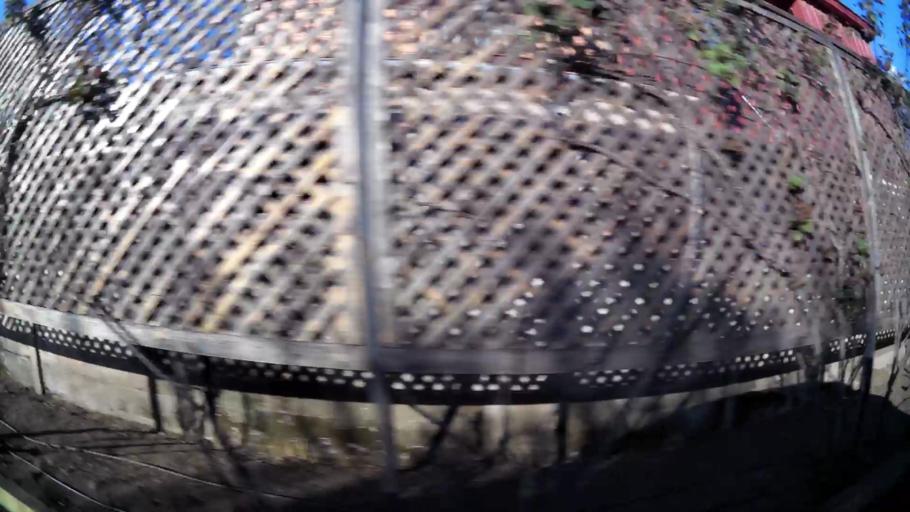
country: CL
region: Santiago Metropolitan
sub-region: Provincia de Santiago
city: Lo Prado
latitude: -33.4807
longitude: -70.7502
